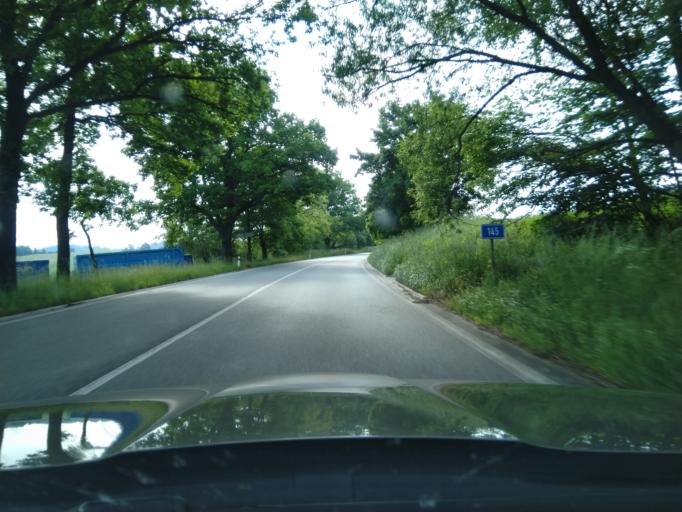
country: CZ
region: Jihocesky
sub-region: Okres Prachatice
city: Strunkovice nad Blanici
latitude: 49.0559
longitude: 14.0902
